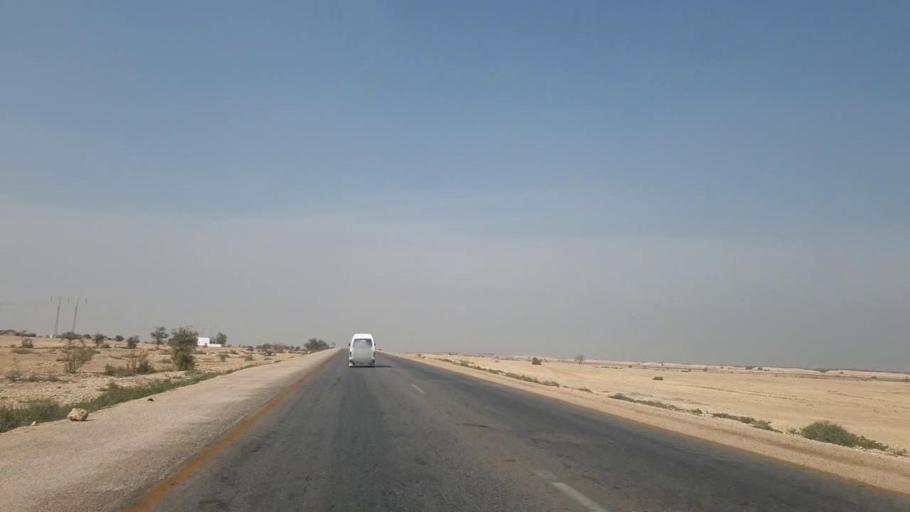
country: PK
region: Sindh
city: Hala
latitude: 25.8409
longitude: 68.2651
